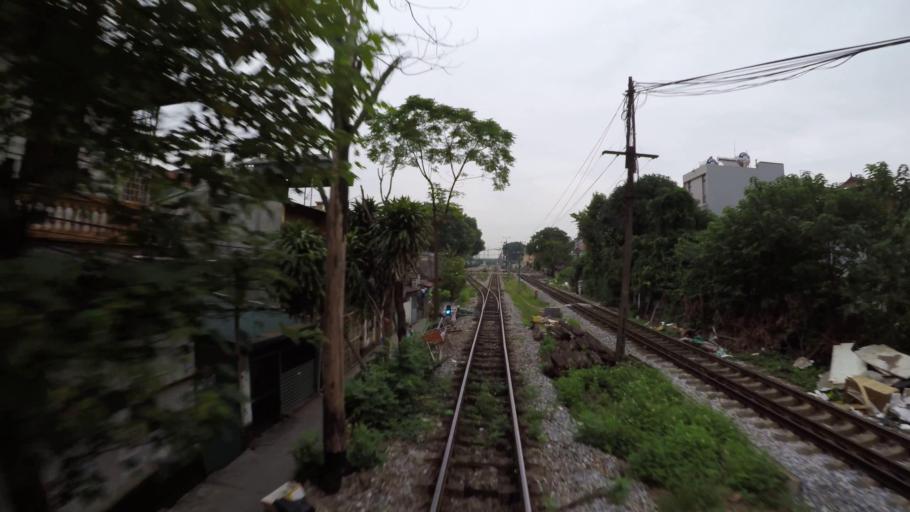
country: VN
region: Ha Noi
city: Trau Quy
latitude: 21.0351
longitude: 105.9028
